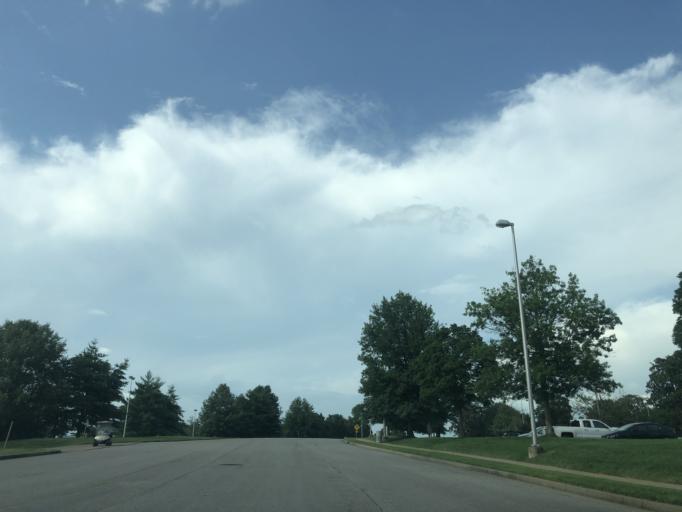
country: US
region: Tennessee
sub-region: Davidson County
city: Oak Hill
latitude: 36.1045
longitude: -86.6797
